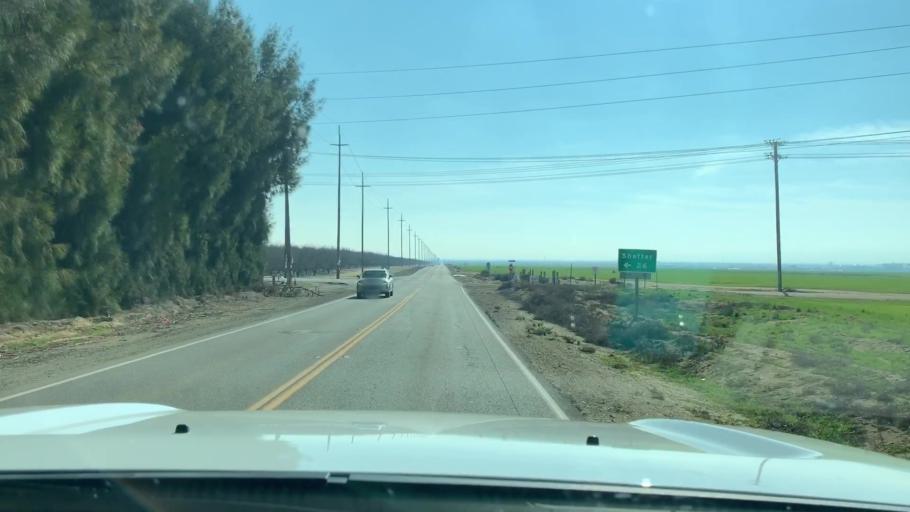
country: US
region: California
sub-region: Kern County
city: Lost Hills
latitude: 35.4996
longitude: -119.7398
